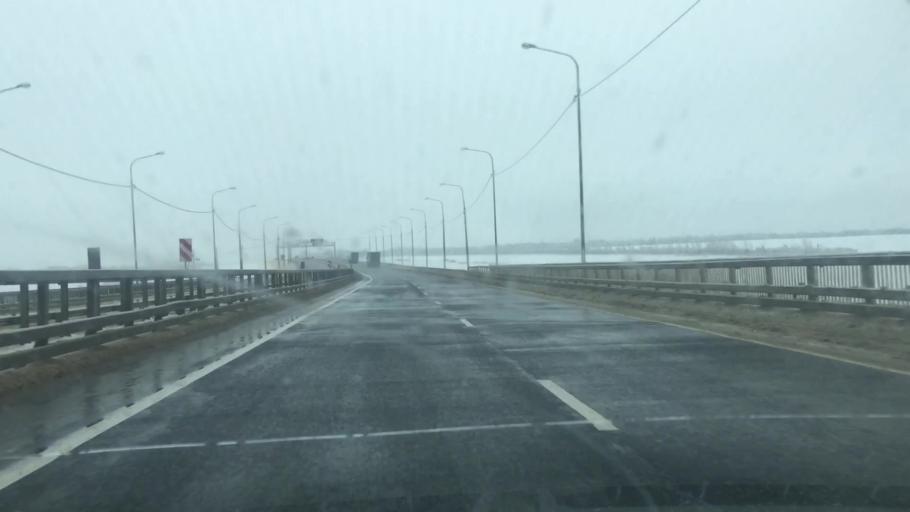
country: RU
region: Lipetsk
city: Stanovoye
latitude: 52.8984
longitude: 38.2244
